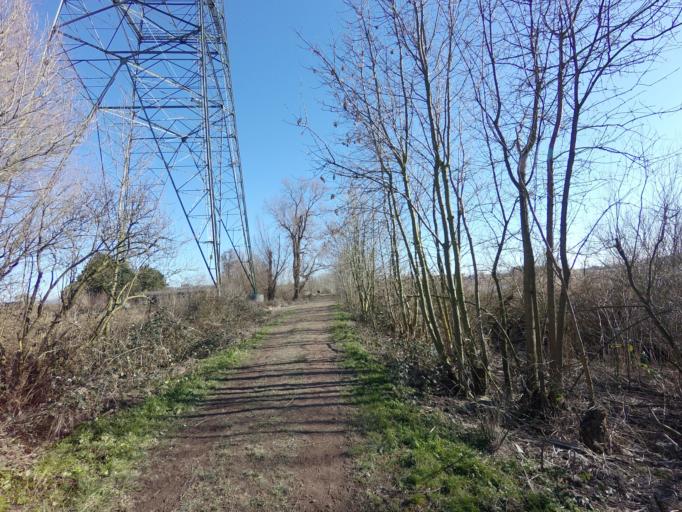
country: NL
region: South Holland
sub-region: Gemeente Krimpen aan den IJssel
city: Krimpen aan den IJssel
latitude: 51.8968
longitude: 4.5971
